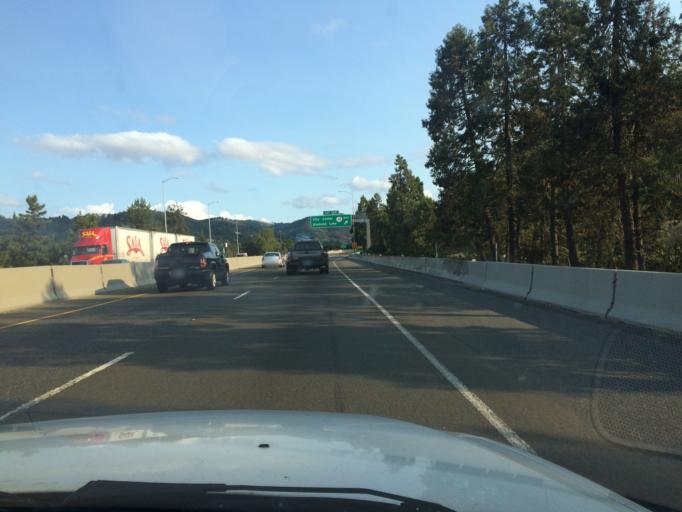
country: US
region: Oregon
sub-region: Douglas County
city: Roseburg
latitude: 43.2156
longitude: -123.3563
